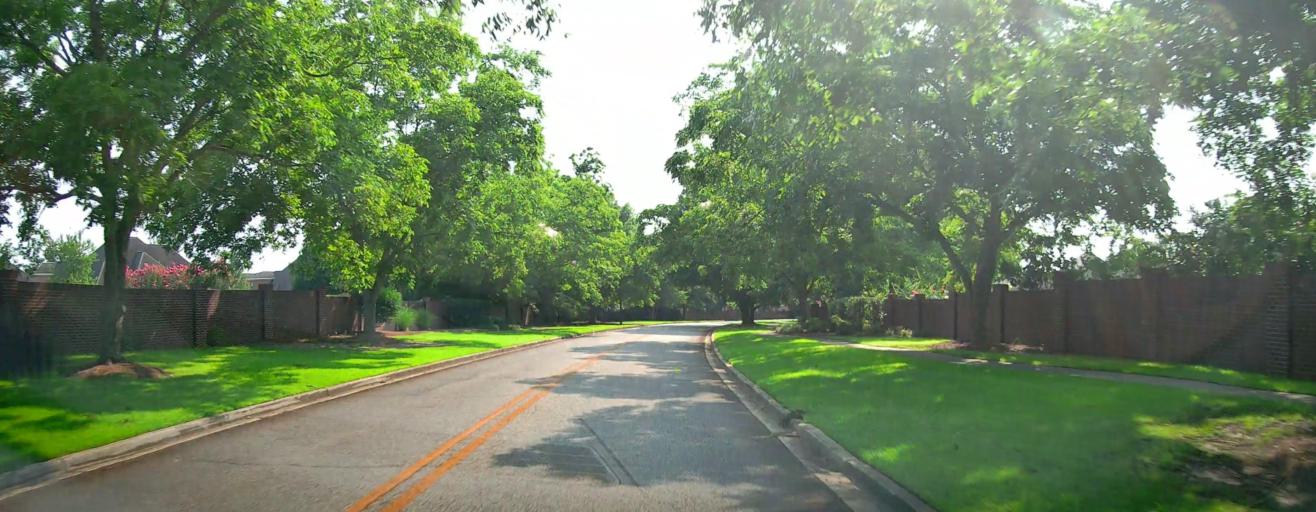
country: US
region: Georgia
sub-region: Houston County
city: Centerville
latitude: 32.6265
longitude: -83.6941
